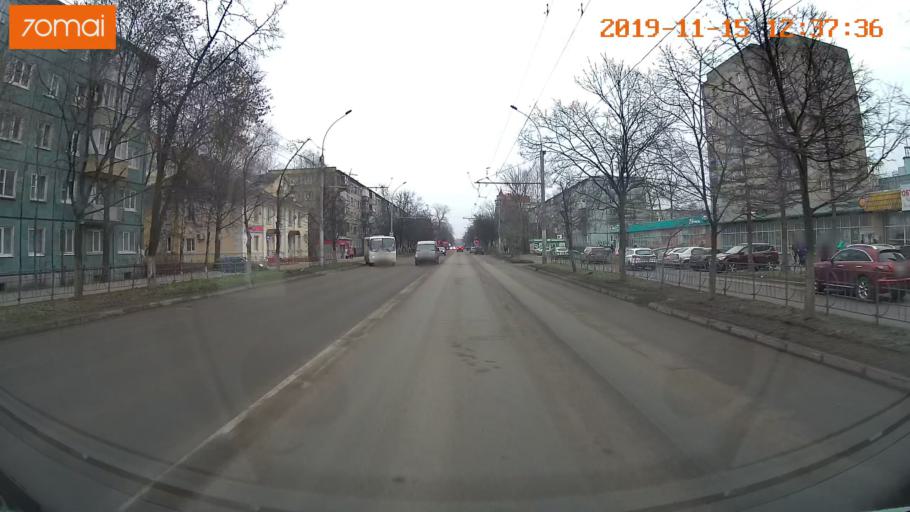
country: RU
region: Vologda
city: Vologda
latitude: 59.2080
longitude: 39.9007
